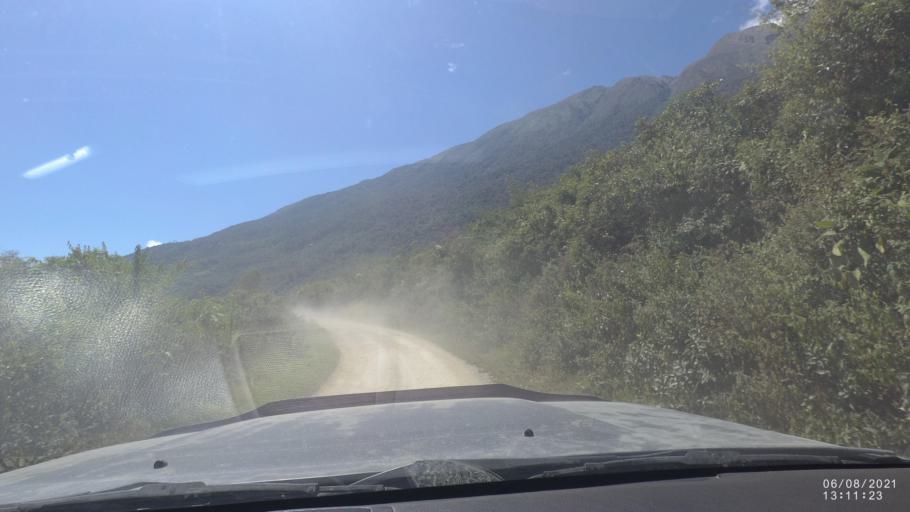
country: BO
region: La Paz
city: Quime
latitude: -16.7200
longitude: -66.7062
